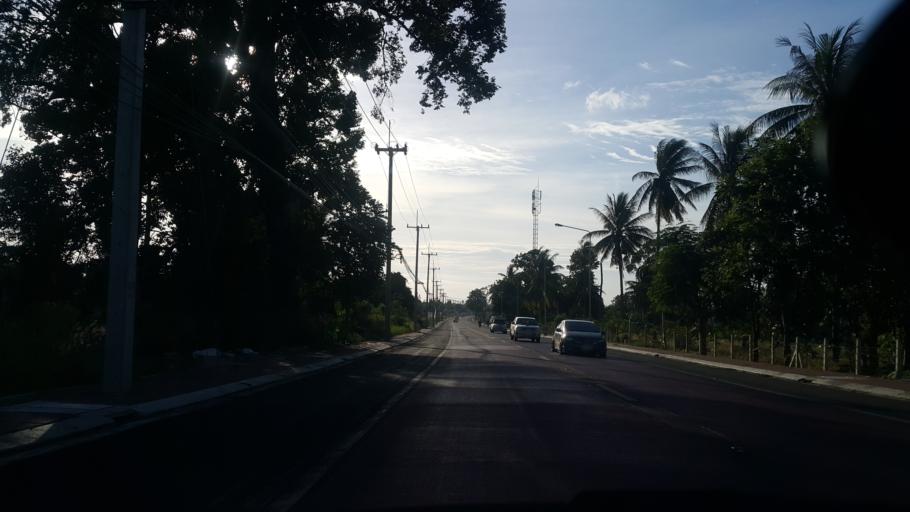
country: TH
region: Chon Buri
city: Sattahip
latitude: 12.7740
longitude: 100.9481
